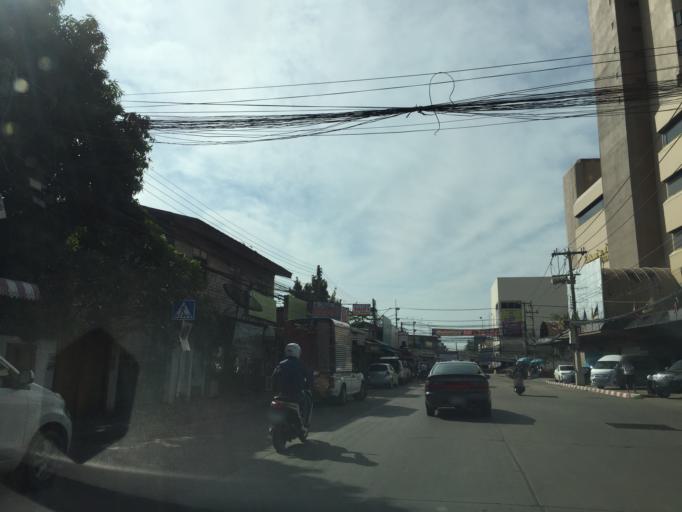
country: TH
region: Phitsanulok
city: Phitsanulok
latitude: 16.8224
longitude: 100.2651
